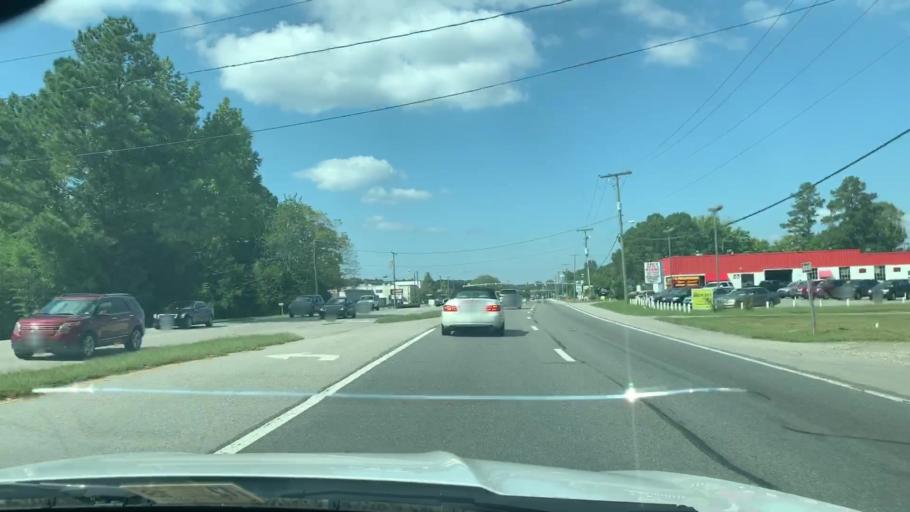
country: US
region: Virginia
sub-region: York County
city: Yorktown
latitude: 37.1690
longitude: -76.4715
